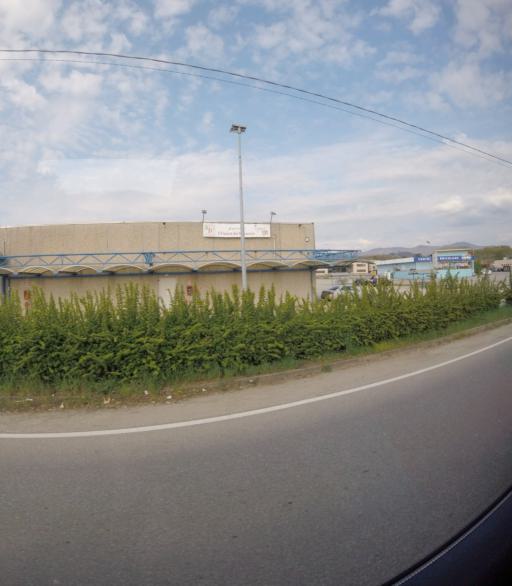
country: IT
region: Piedmont
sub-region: Provincia di Novara
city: Gozzano
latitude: 45.7346
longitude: 8.4407
